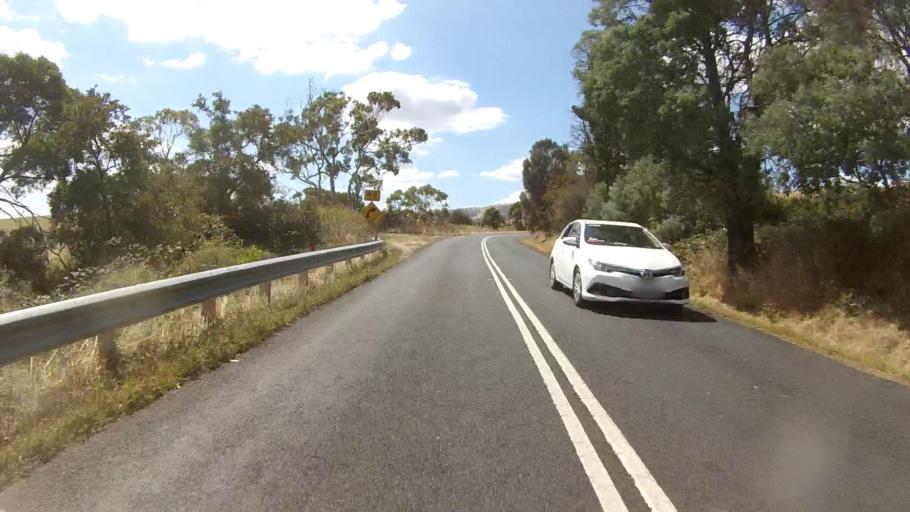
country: AU
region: Tasmania
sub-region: Derwent Valley
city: New Norfolk
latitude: -42.7334
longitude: 146.9231
